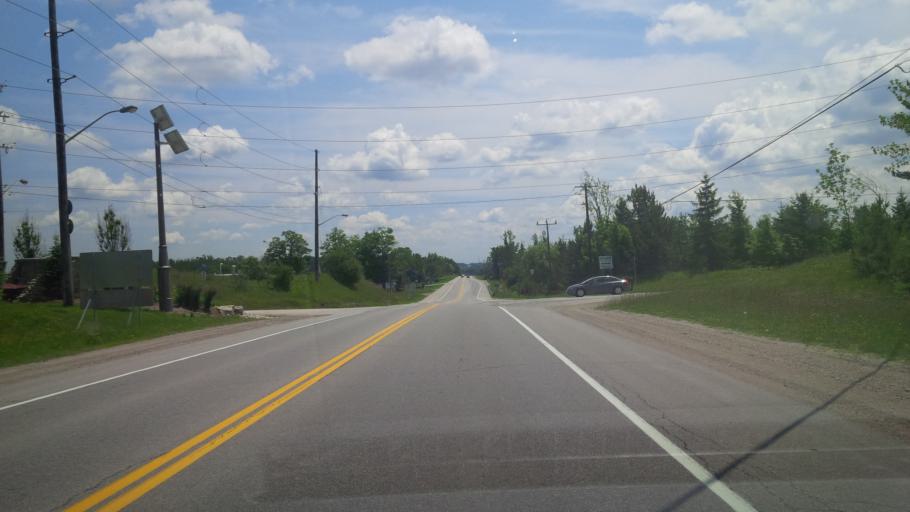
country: CA
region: Ontario
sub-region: Wellington County
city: Guelph
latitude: 43.4876
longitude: -80.1716
